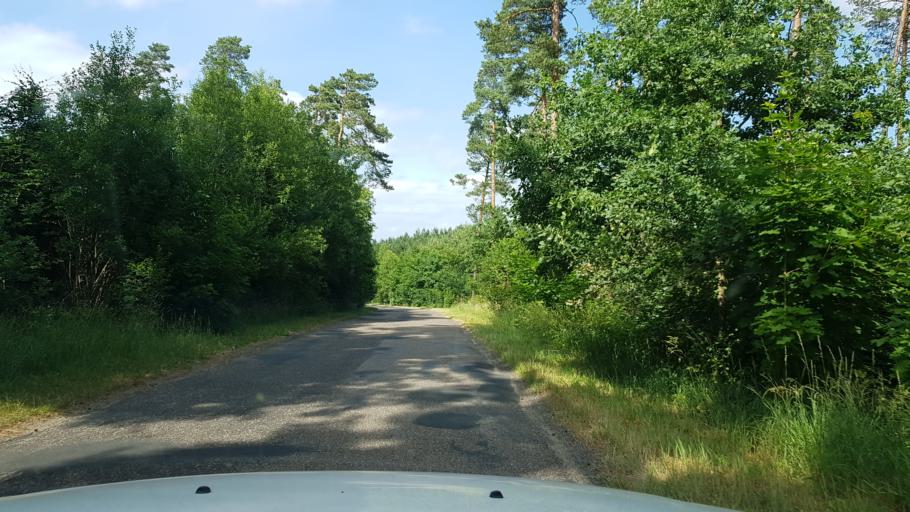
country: PL
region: West Pomeranian Voivodeship
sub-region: Powiat goleniowski
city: Mosty
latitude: 53.5519
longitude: 14.9640
